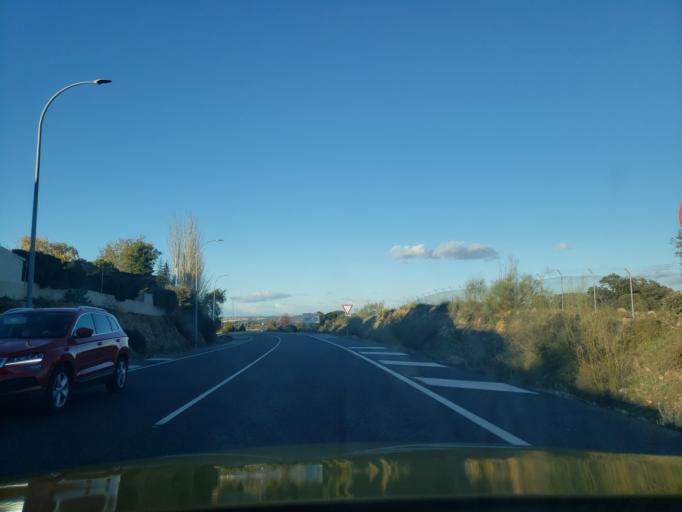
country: ES
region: Castille-La Mancha
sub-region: Province of Toledo
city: Cobisa
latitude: 39.8264
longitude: -4.0179
